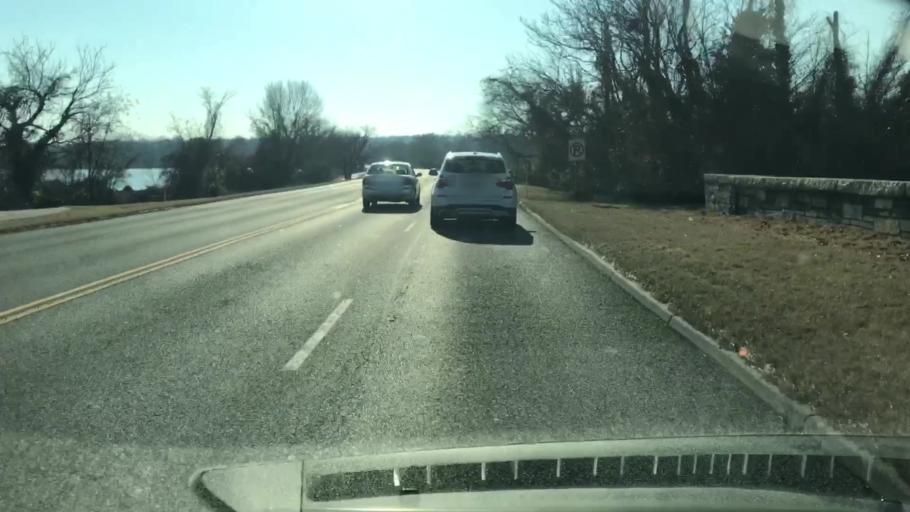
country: US
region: Virginia
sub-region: Fairfax County
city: Belle Haven
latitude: 38.7899
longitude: -77.0515
